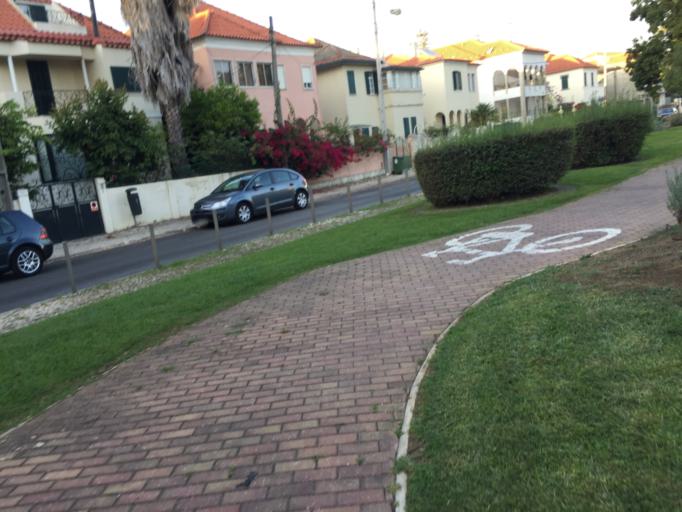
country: PT
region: Lisbon
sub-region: Odivelas
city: Olival do Basto
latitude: 38.7585
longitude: -9.1671
